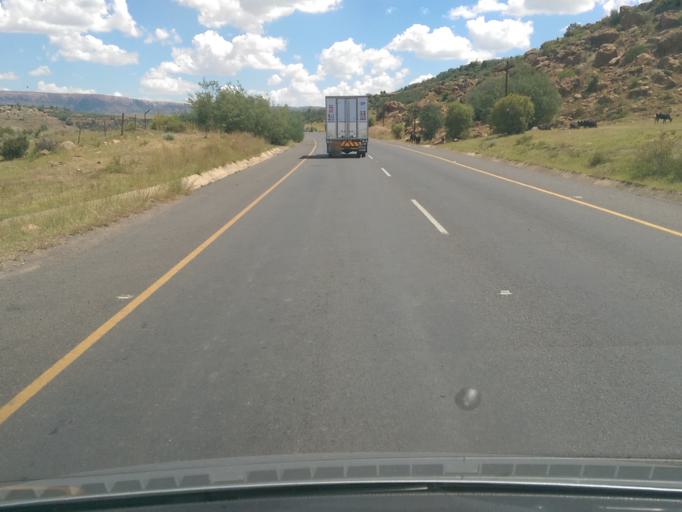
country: LS
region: Maseru
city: Maseru
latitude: -29.3955
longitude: 27.5386
